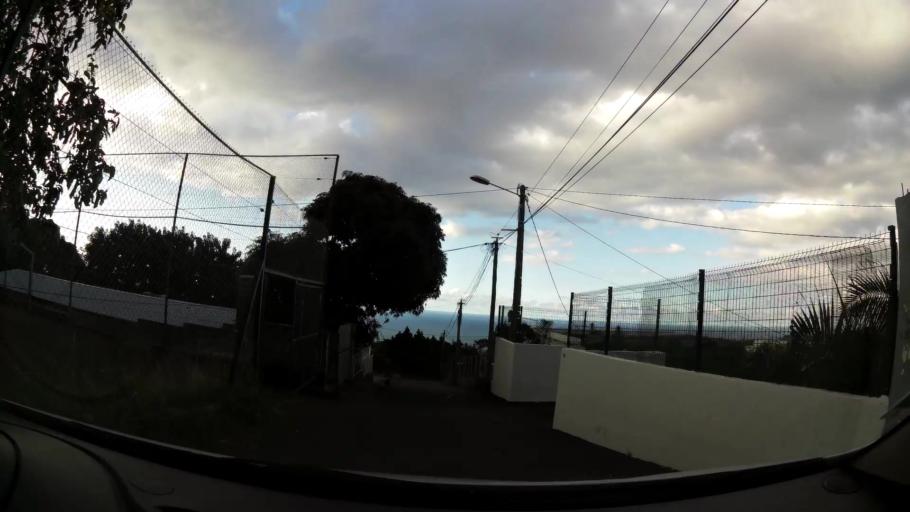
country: RE
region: Reunion
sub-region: Reunion
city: Saint-Denis
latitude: -20.9005
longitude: 55.4454
